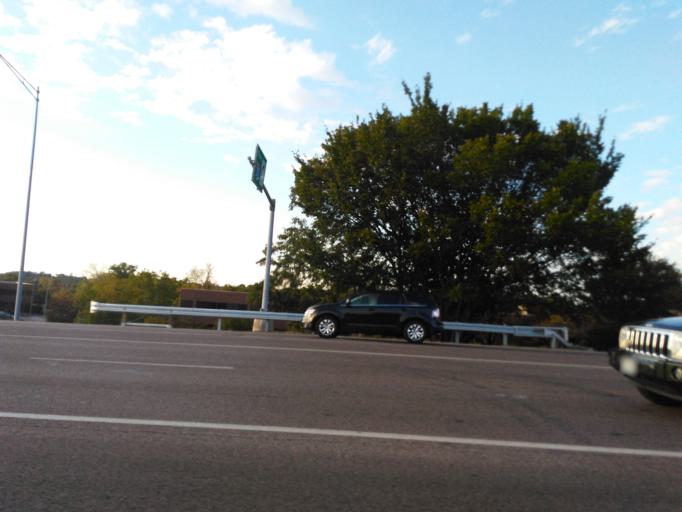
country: US
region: Missouri
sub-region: Saint Louis County
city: Sunset Hills
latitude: 38.5256
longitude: -90.3975
